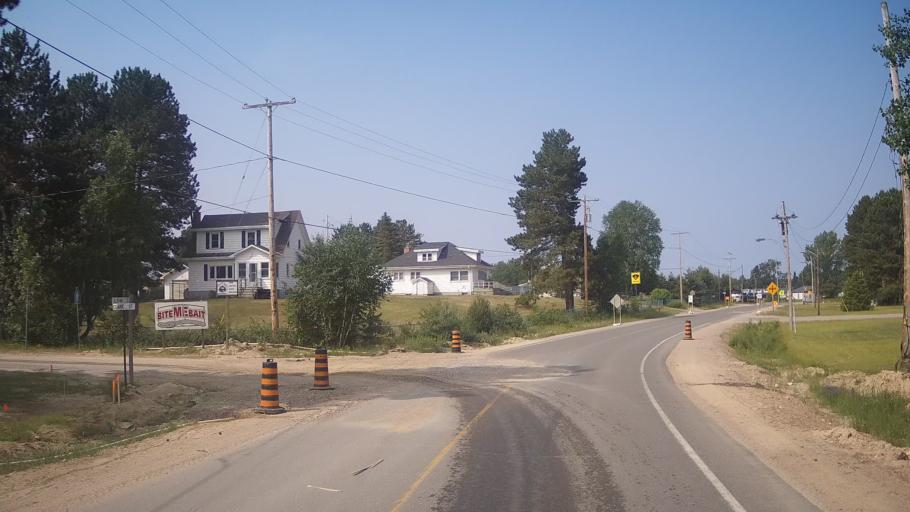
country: CA
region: Ontario
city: Timmins
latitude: 47.6758
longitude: -81.7197
